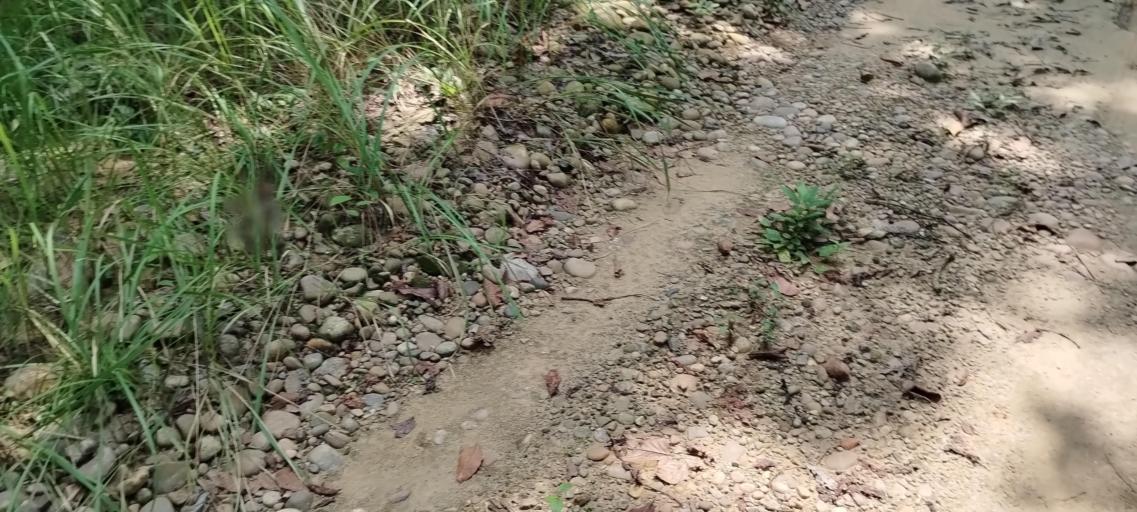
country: NP
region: Far Western
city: Tikapur
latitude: 28.4996
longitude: 81.2560
